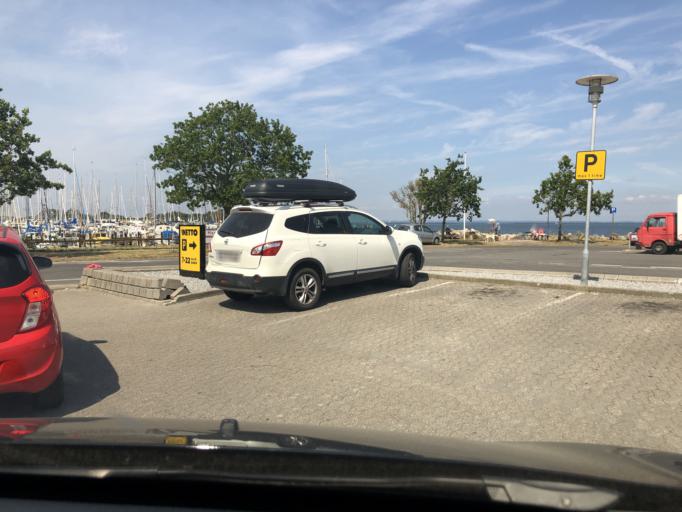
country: DK
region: South Denmark
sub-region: AEro Kommune
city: AEroskobing
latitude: 54.8919
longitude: 10.4110
